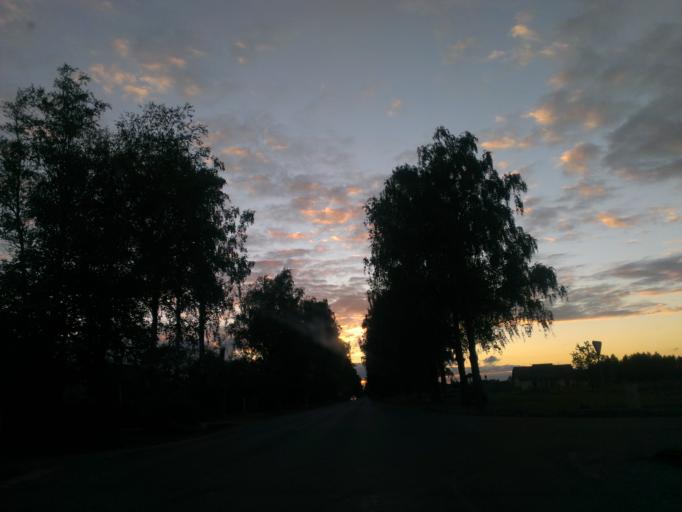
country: LV
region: Vecumnieki
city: Vecumnieki
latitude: 56.6108
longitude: 24.5145
